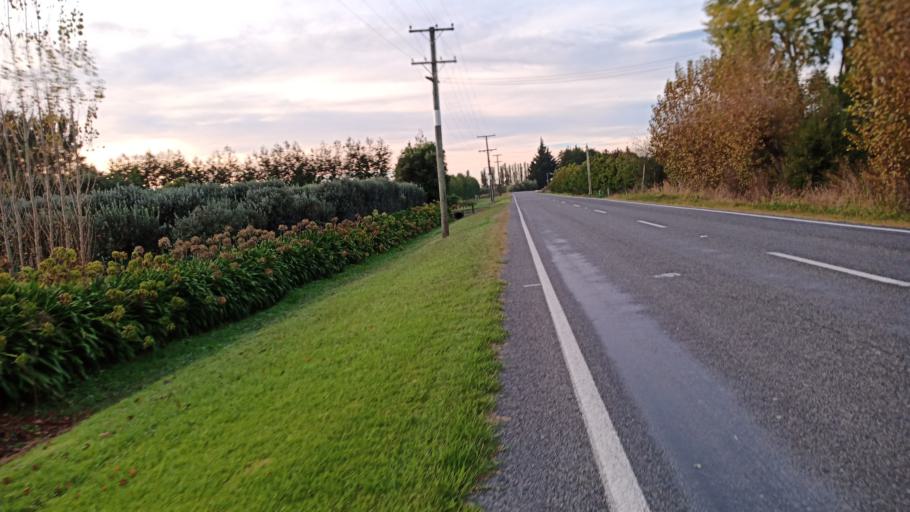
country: NZ
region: Gisborne
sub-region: Gisborne District
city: Gisborne
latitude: -38.6495
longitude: 177.9490
